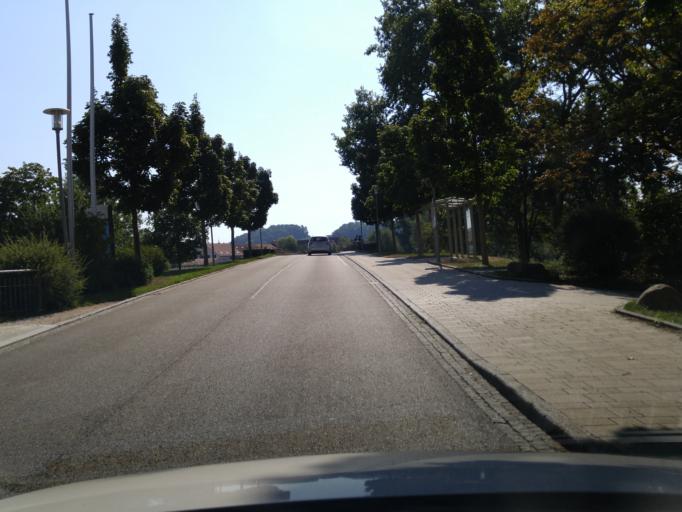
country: DE
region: Baden-Wuerttemberg
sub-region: Regierungsbezirk Stuttgart
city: Neckartailfingen
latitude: 48.6116
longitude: 9.2639
